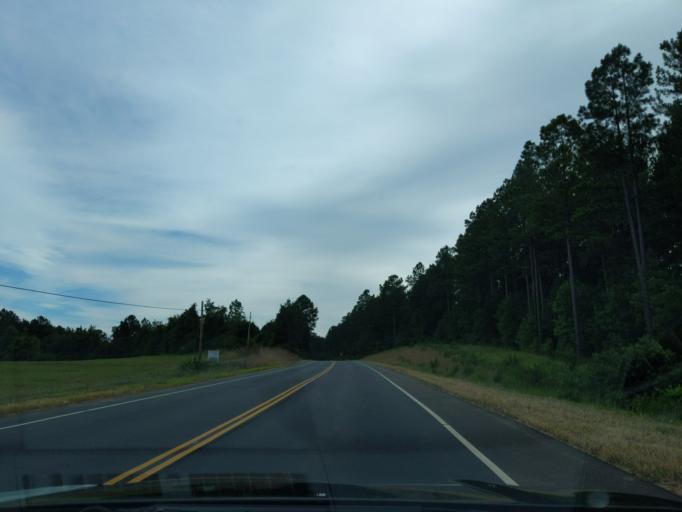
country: US
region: North Carolina
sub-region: Cabarrus County
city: Mount Pleasant
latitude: 35.4248
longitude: -80.4143
